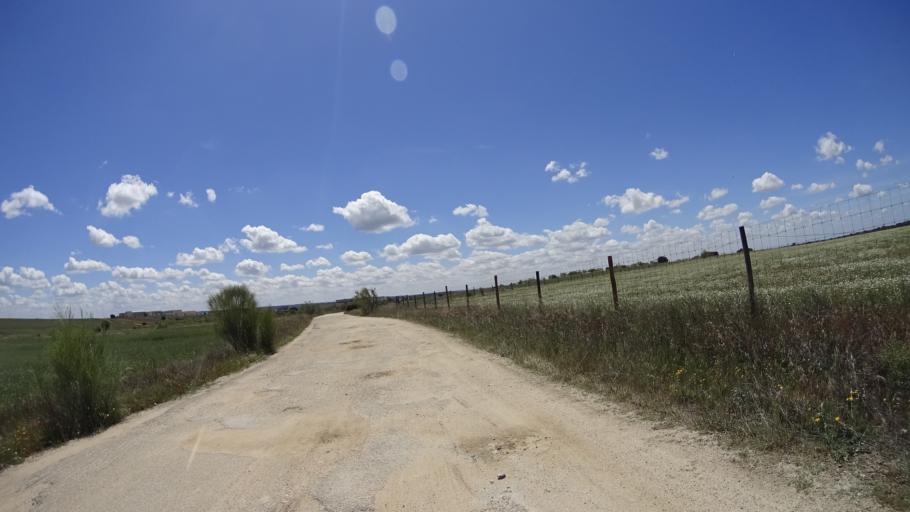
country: ES
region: Madrid
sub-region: Provincia de Madrid
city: Villanueva del Pardillo
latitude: 40.4952
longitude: -3.9914
